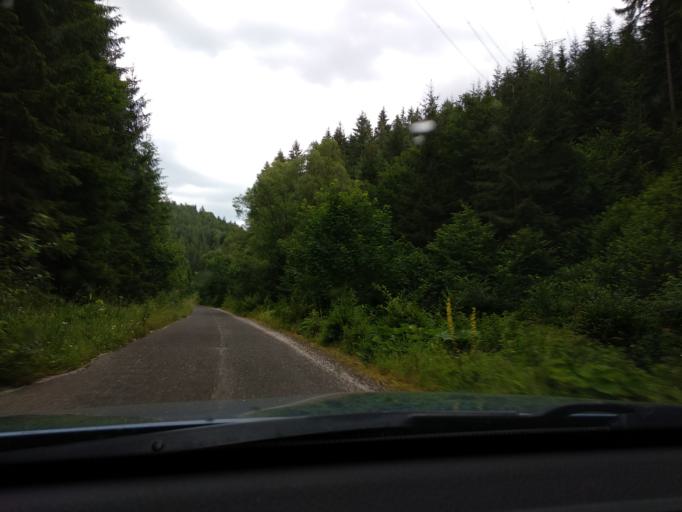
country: SK
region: Zilinsky
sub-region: Okres Liptovsky Mikulas
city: Hybe
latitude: 49.0170
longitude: 19.8649
